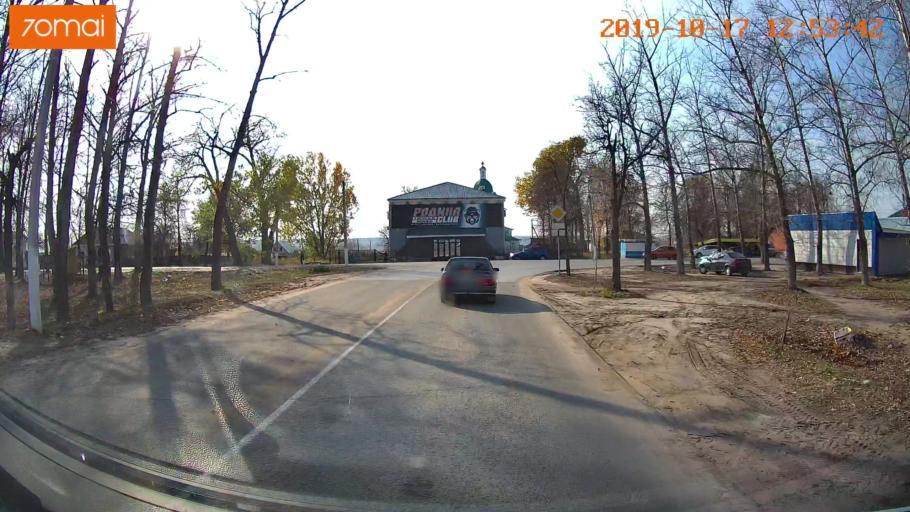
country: RU
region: Rjazan
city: Kasimov
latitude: 54.9421
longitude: 41.3814
